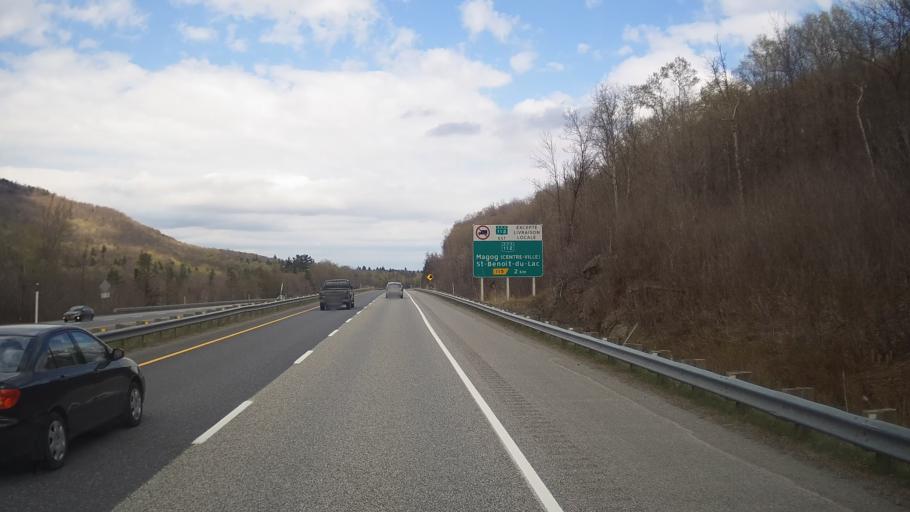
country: CA
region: Quebec
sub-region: Estrie
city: Magog
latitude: 45.2901
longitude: -72.2443
